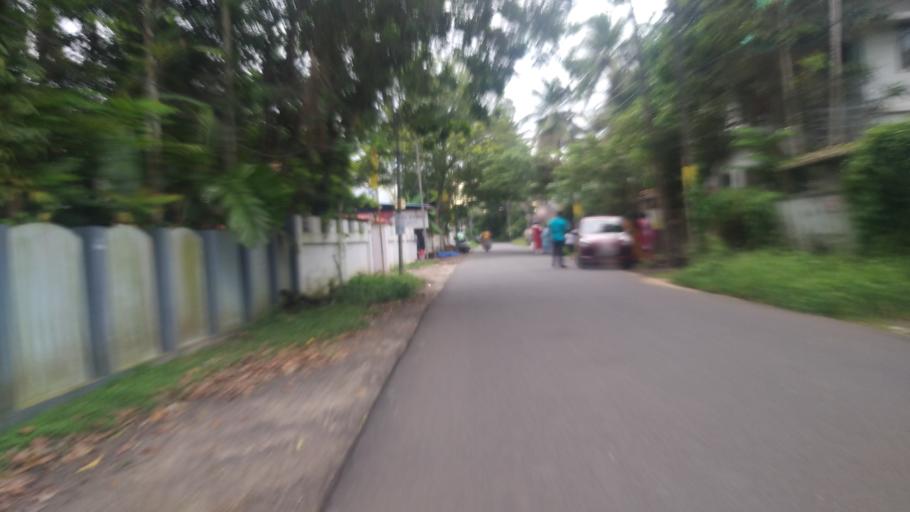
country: IN
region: Kerala
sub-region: Alappuzha
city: Arukutti
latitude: 9.8610
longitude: 76.2893
